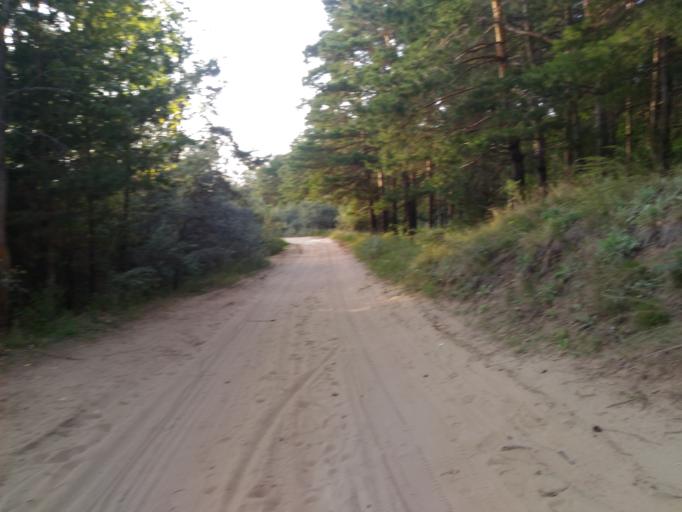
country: RU
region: Ulyanovsk
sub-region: Ulyanovskiy Rayon
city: Ulyanovsk
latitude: 54.3579
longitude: 48.5144
